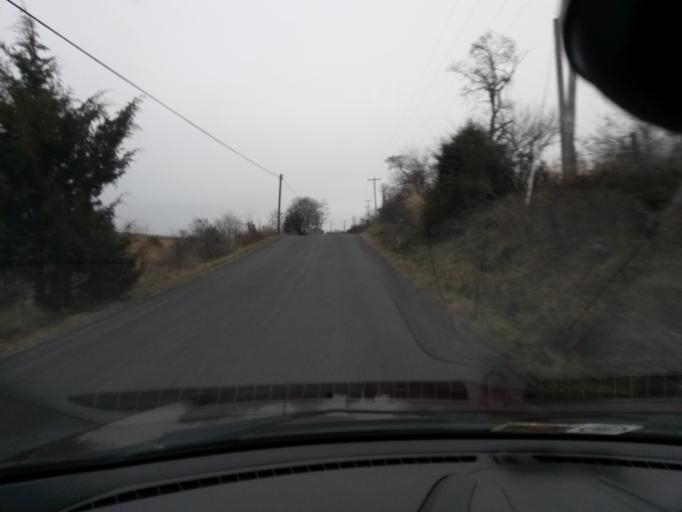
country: US
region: Virginia
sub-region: Rockbridge County
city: East Lexington
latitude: 37.9420
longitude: -79.2495
